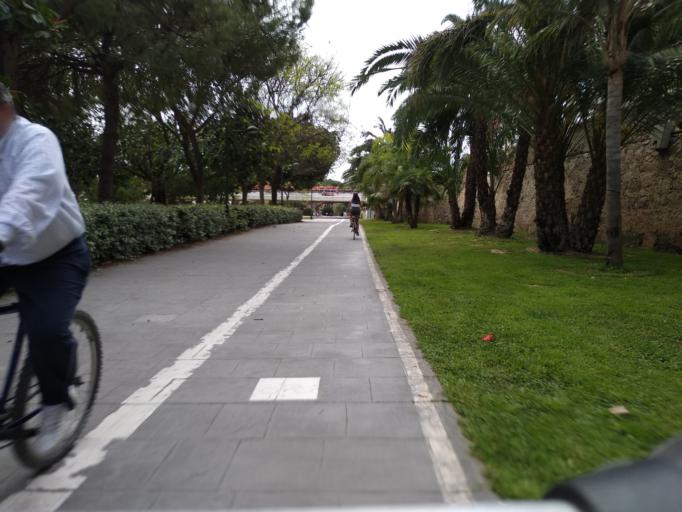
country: ES
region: Valencia
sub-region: Provincia de Valencia
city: Valencia
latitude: 39.4715
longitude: -0.3657
